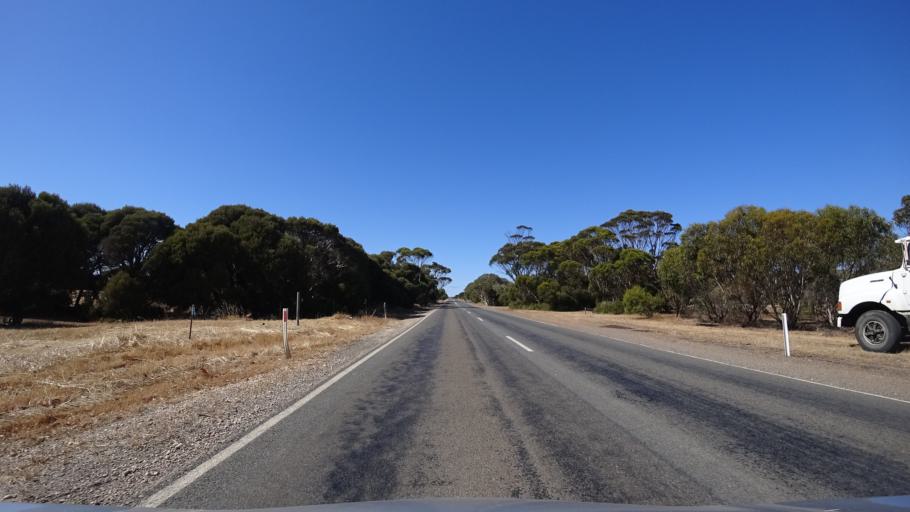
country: AU
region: South Australia
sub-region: Kangaroo Island
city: Kingscote
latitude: -35.6823
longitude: 137.5729
